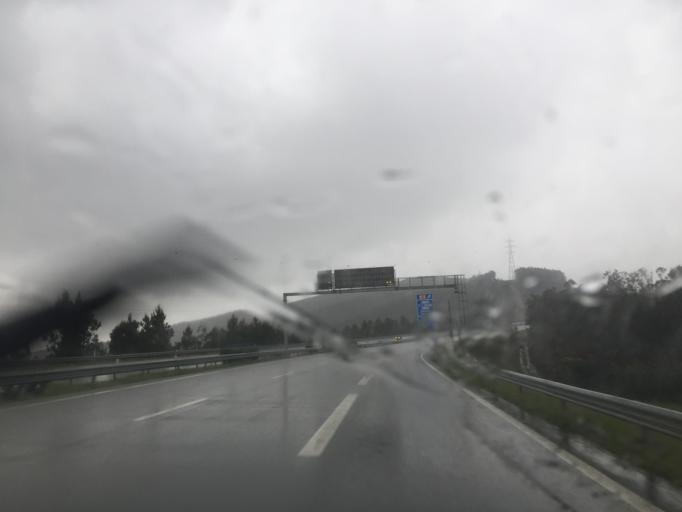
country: PT
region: Aveiro
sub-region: Sever do Vouga
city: Sever do Vouga
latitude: 40.6582
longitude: -8.3597
